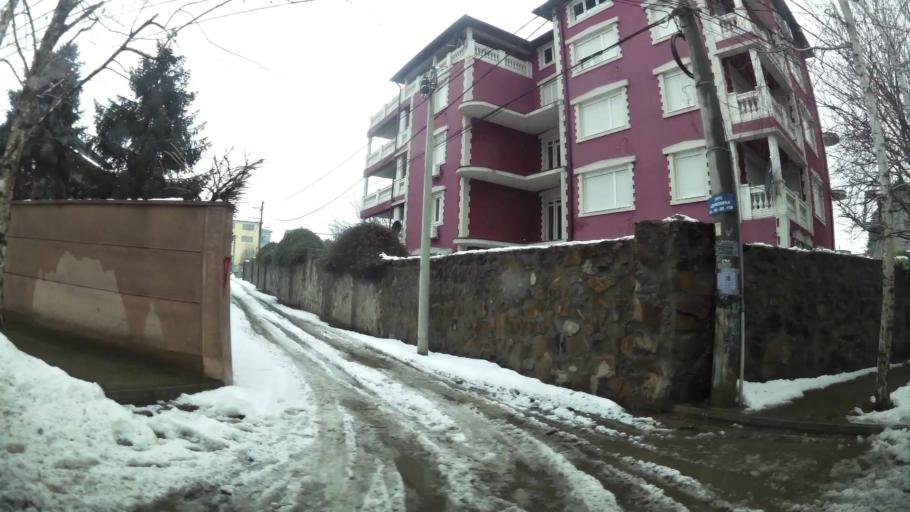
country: RS
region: Central Serbia
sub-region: Belgrade
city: Zemun
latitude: 44.8505
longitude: 20.3574
